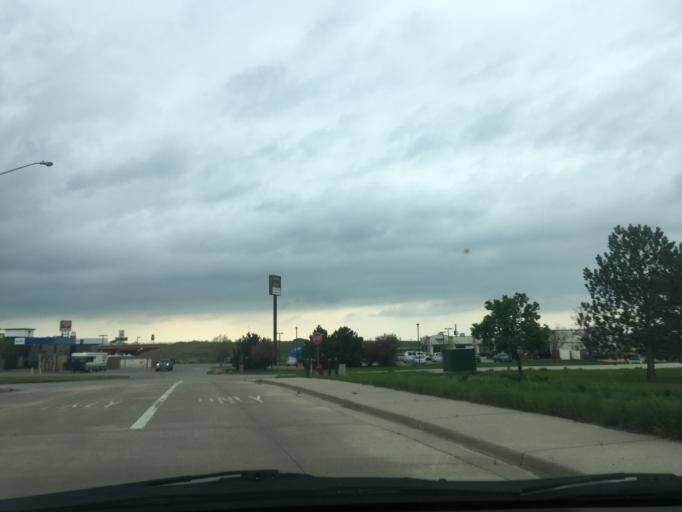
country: US
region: Colorado
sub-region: Weld County
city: Firestone
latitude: 40.1631
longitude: -104.9757
